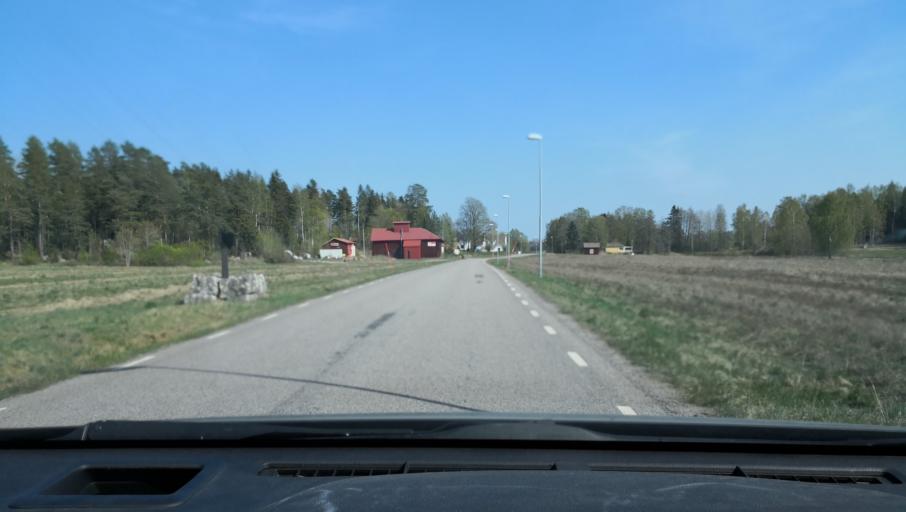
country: SE
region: Uppsala
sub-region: Heby Kommun
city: Heby
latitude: 60.0354
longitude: 16.7894
